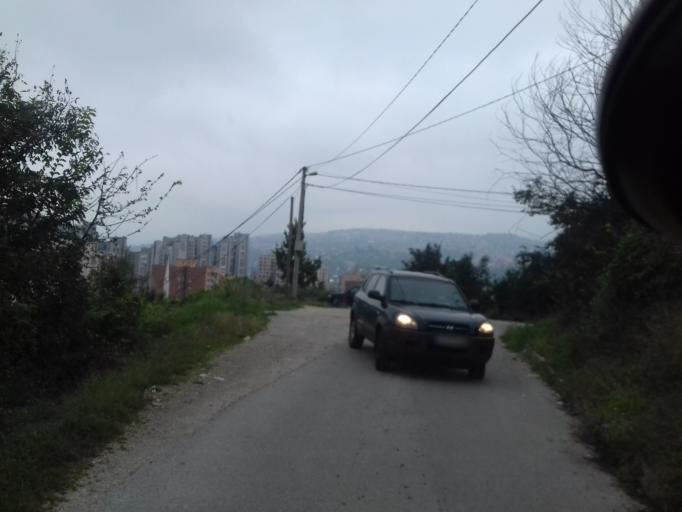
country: BA
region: Federation of Bosnia and Herzegovina
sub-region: Kanton Sarajevo
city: Sarajevo
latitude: 43.8399
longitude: 18.3537
